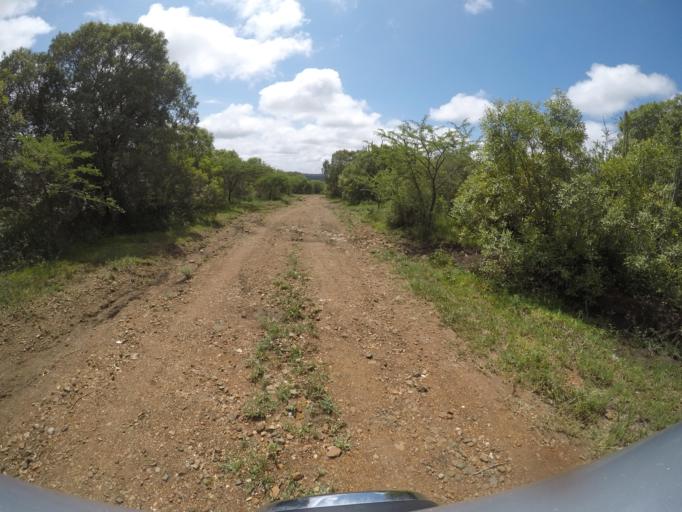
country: ZA
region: KwaZulu-Natal
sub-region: uThungulu District Municipality
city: Empangeni
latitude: -28.5728
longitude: 31.8303
